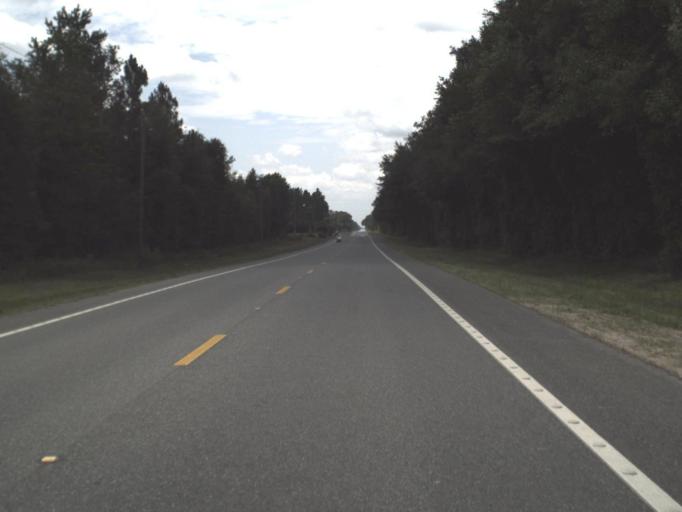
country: US
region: Florida
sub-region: Suwannee County
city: Wellborn
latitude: 30.1136
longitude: -82.9489
